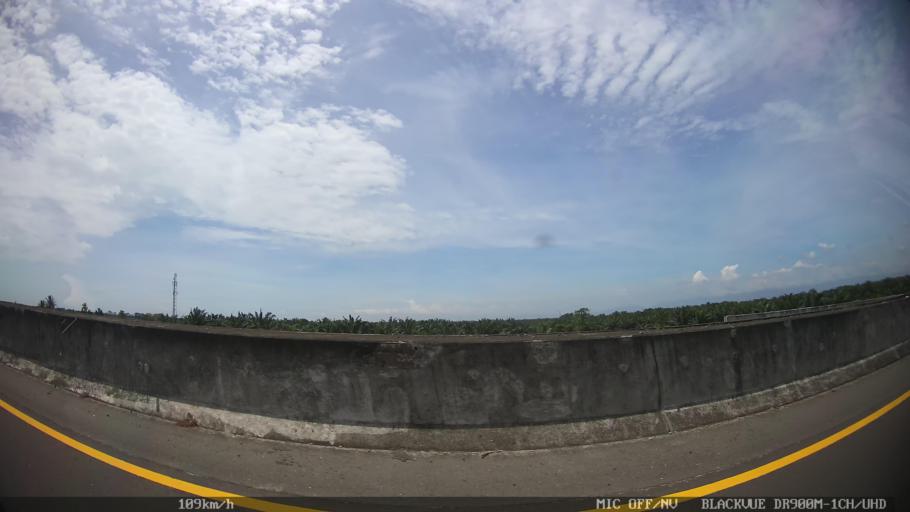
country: ID
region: North Sumatra
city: Perbaungan
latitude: 3.5316
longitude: 98.8855
